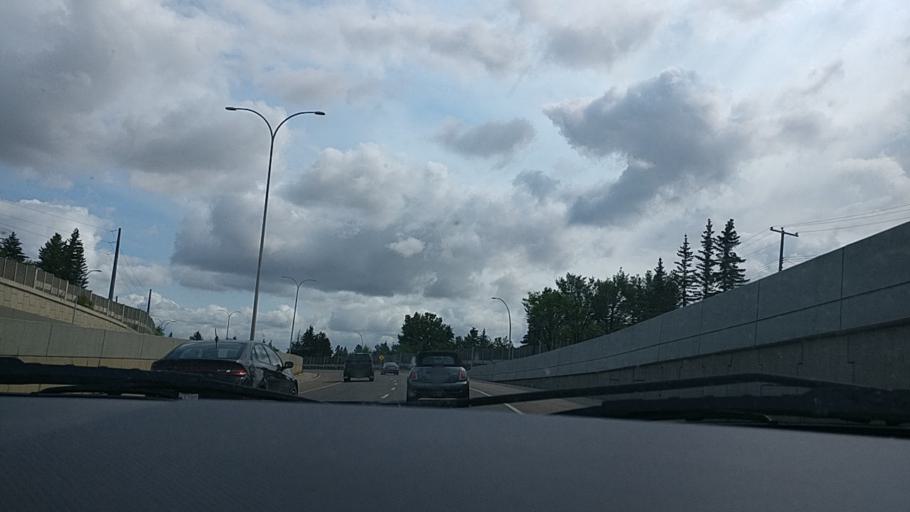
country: CA
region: Alberta
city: Calgary
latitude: 51.0896
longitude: -114.0933
